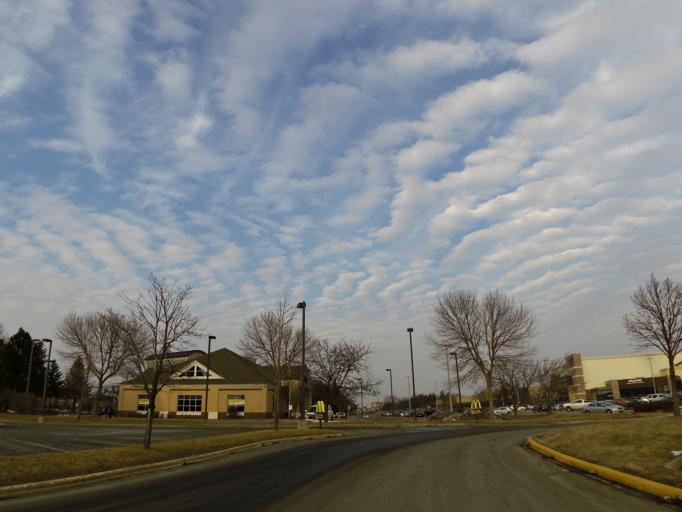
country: US
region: Minnesota
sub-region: Hennepin County
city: Eden Prairie
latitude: 44.8535
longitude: -93.4294
